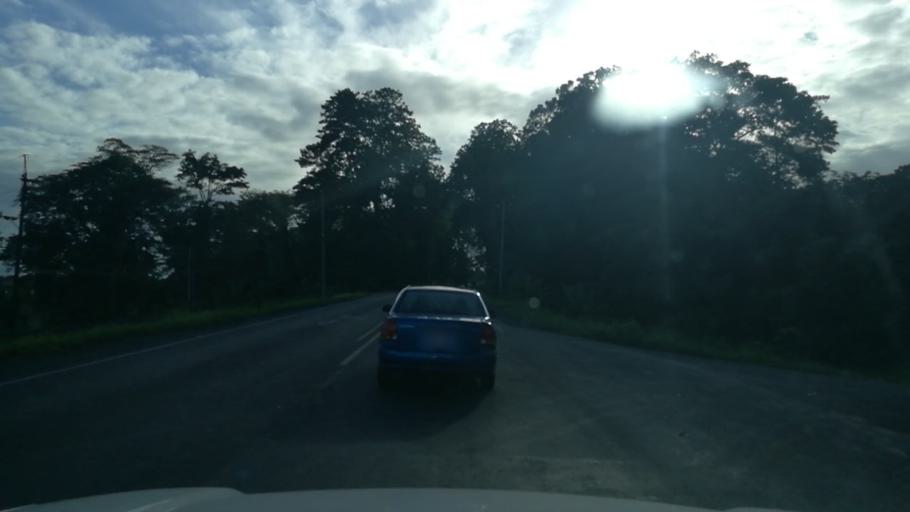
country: CR
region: Limon
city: Matina
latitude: 10.0447
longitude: -83.2815
